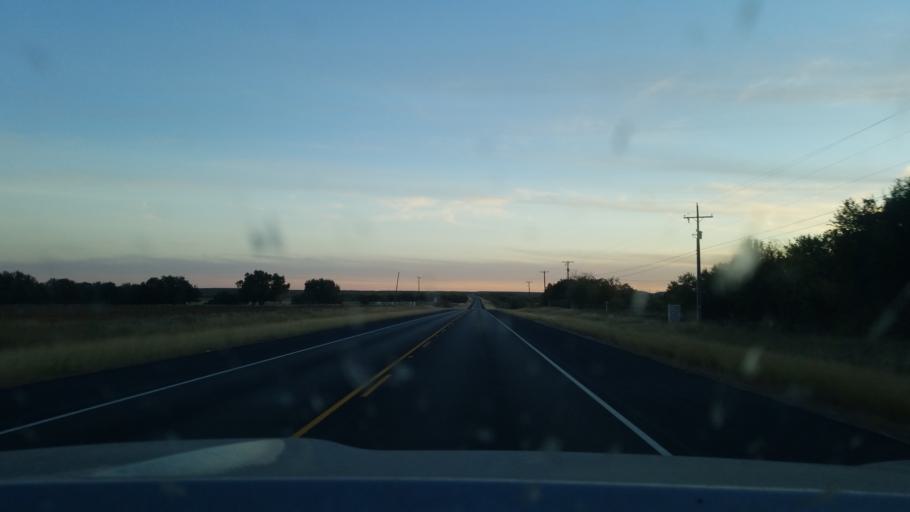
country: US
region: Texas
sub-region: Stephens County
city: Breckenridge
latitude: 32.6599
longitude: -98.9023
